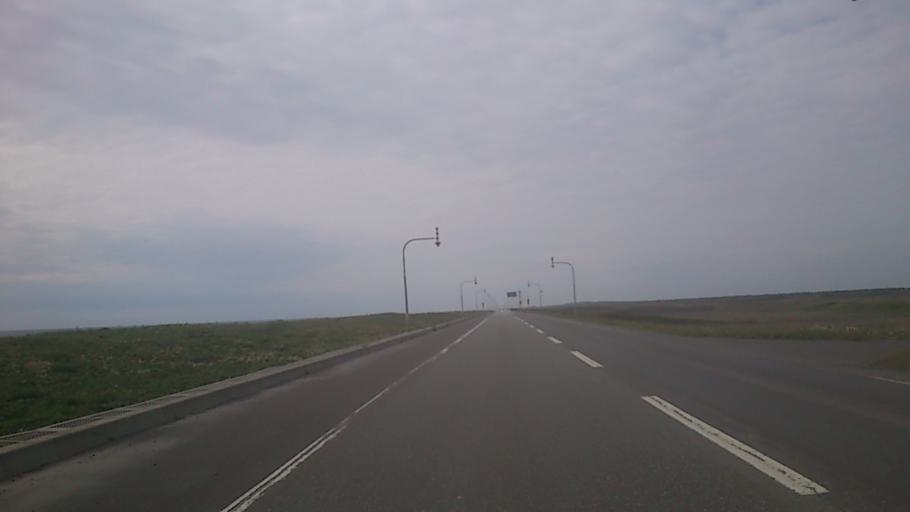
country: JP
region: Hokkaido
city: Makubetsu
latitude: 45.0065
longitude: 141.6790
